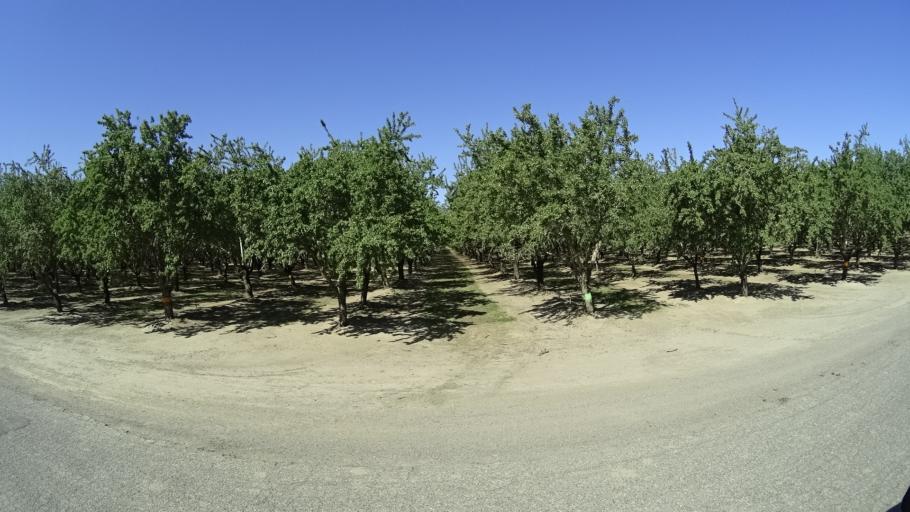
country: US
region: California
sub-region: Glenn County
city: Hamilton City
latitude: 39.7422
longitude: -122.0573
